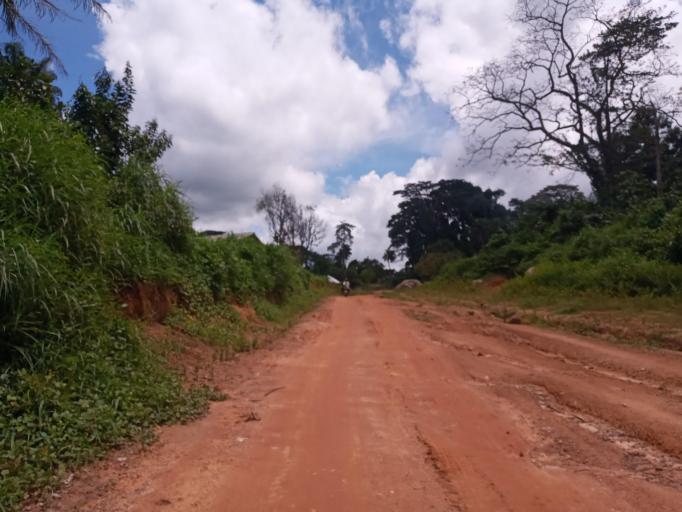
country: SL
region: Eastern Province
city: Tombu
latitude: 8.6288
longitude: -10.8349
